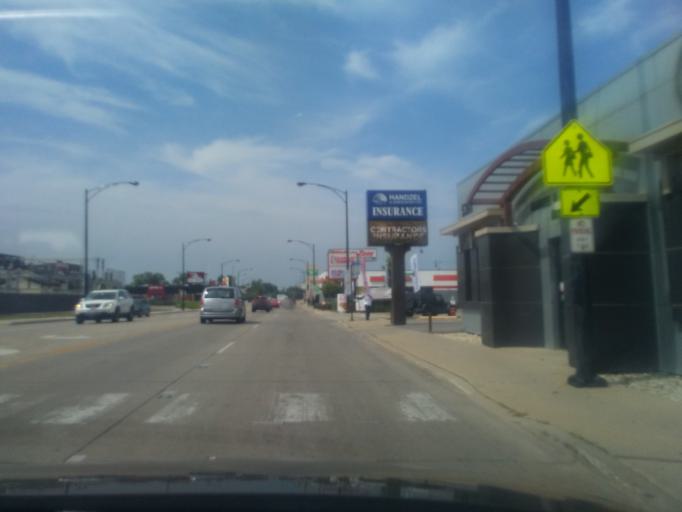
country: US
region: Illinois
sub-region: Cook County
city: Harwood Heights
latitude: 41.9788
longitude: -87.8069
